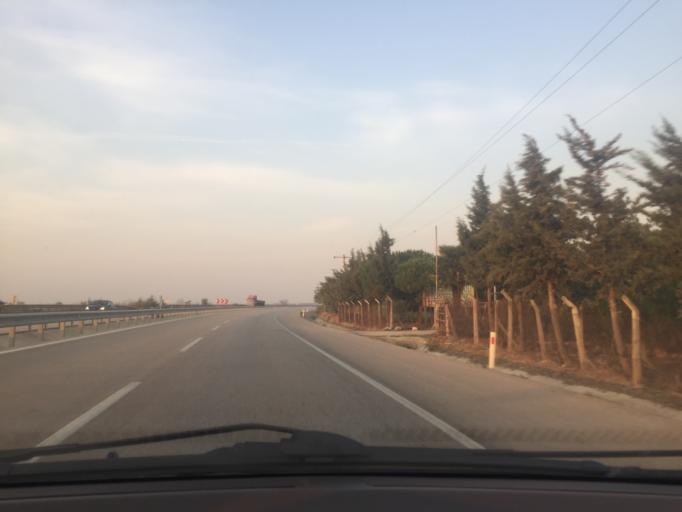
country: TR
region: Bursa
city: Karacabey
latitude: 40.2376
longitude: 28.3049
